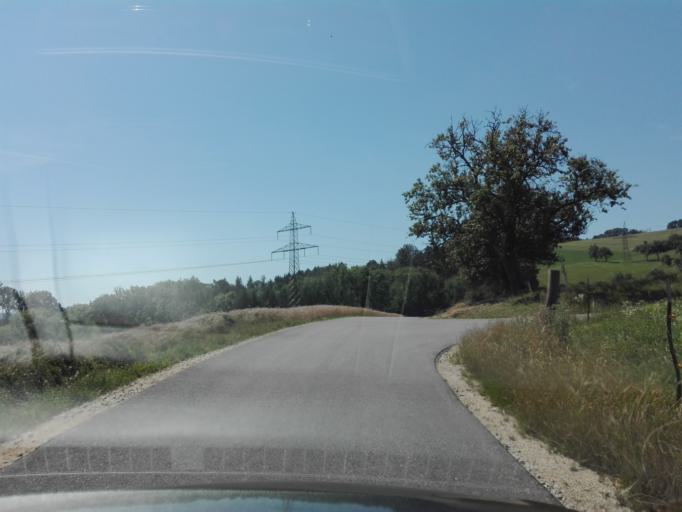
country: AT
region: Upper Austria
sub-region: Politischer Bezirk Urfahr-Umgebung
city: Steyregg
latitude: 48.3098
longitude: 14.3907
